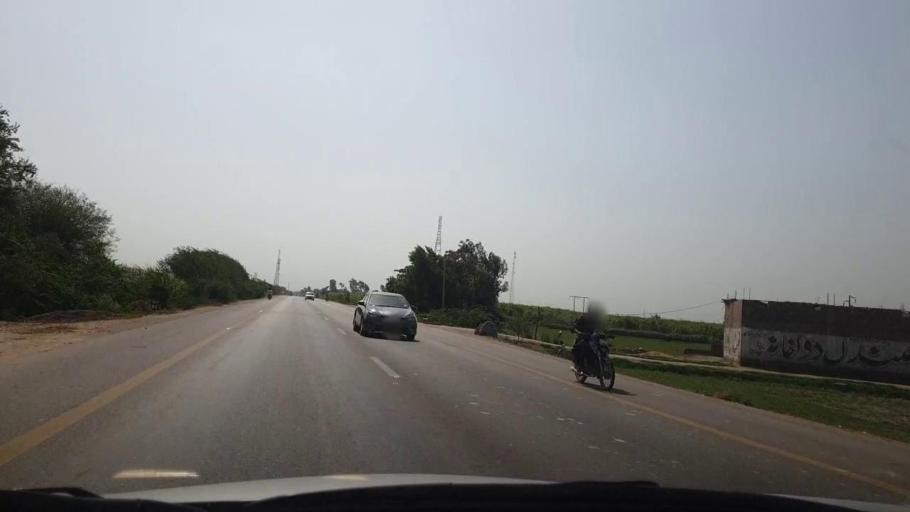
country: PK
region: Sindh
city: Tando Muhammad Khan
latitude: 25.0961
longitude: 68.5946
